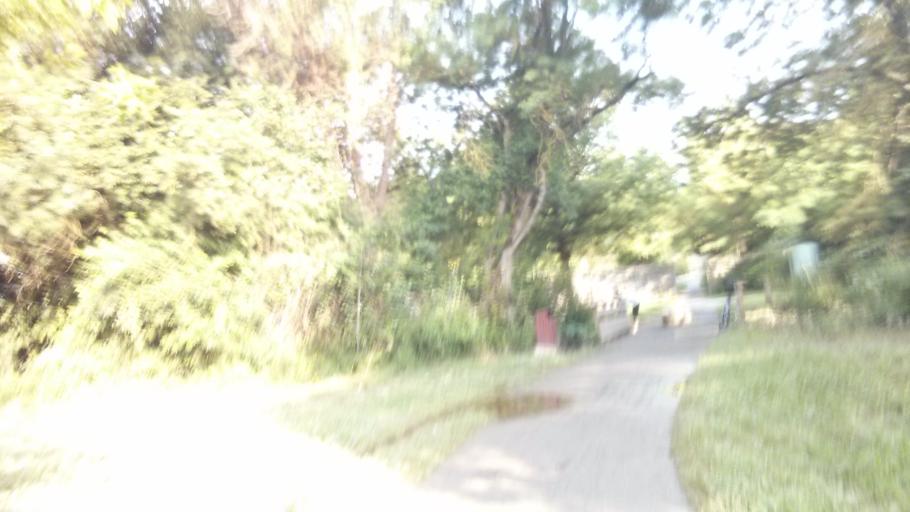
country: FR
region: Pays de la Loire
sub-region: Departement de la Loire-Atlantique
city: Reze
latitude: 47.1830
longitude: -1.5297
